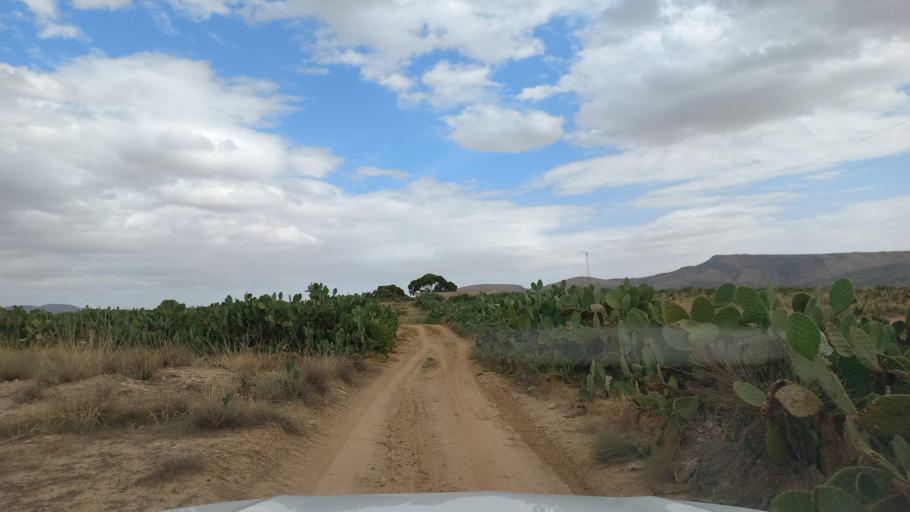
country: TN
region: Al Qasrayn
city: Sbiba
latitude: 35.3788
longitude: 9.1275
